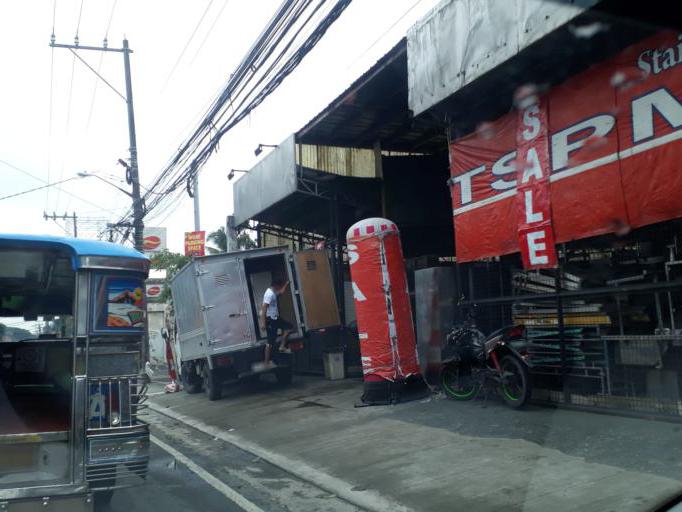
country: PH
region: Calabarzon
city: Del Monte
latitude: 14.6484
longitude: 121.0176
